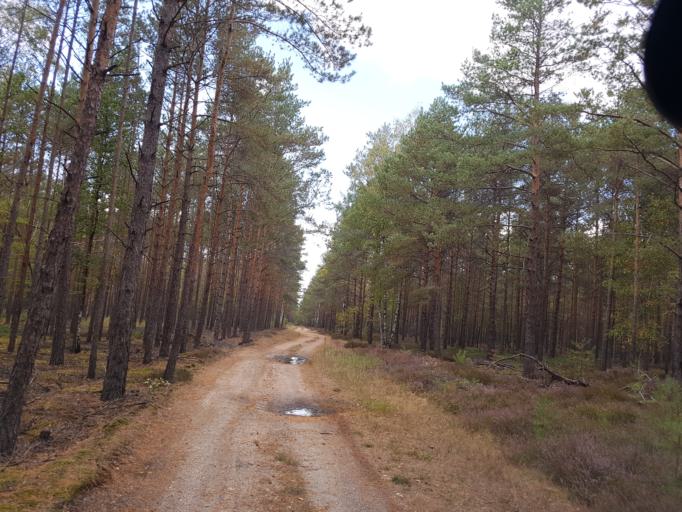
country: DE
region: Brandenburg
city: Finsterwalde
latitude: 51.5885
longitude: 13.7554
